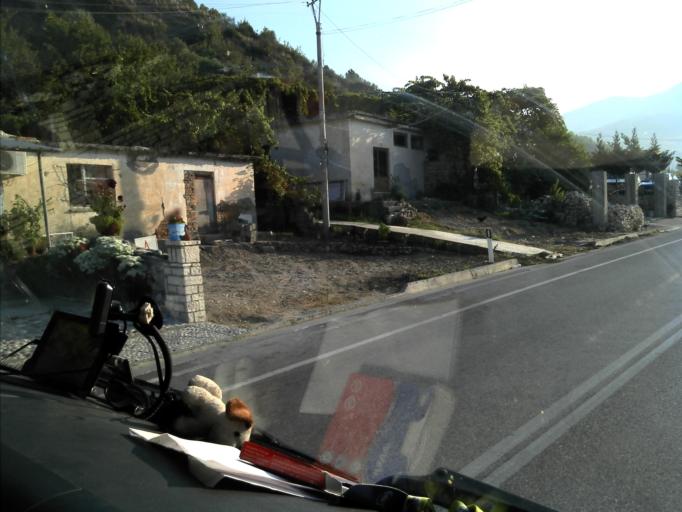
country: AL
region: Gjirokaster
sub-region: Rrethi i Tepelenes
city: Memaliaj
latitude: 40.3532
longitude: 19.9701
